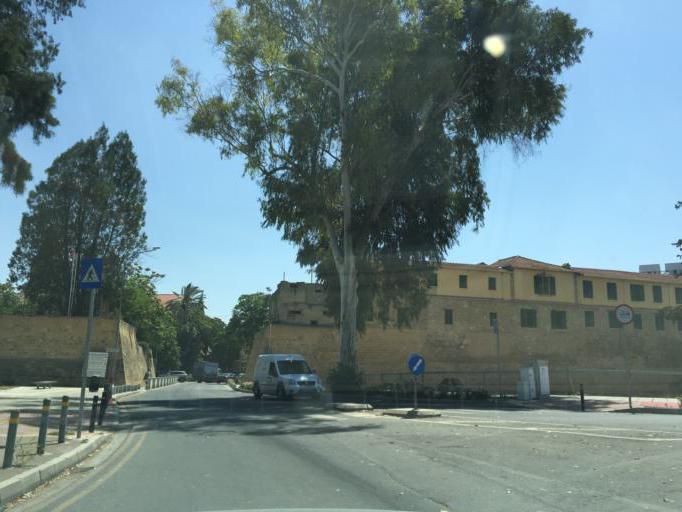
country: CY
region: Lefkosia
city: Nicosia
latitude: 35.1738
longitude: 33.3561
